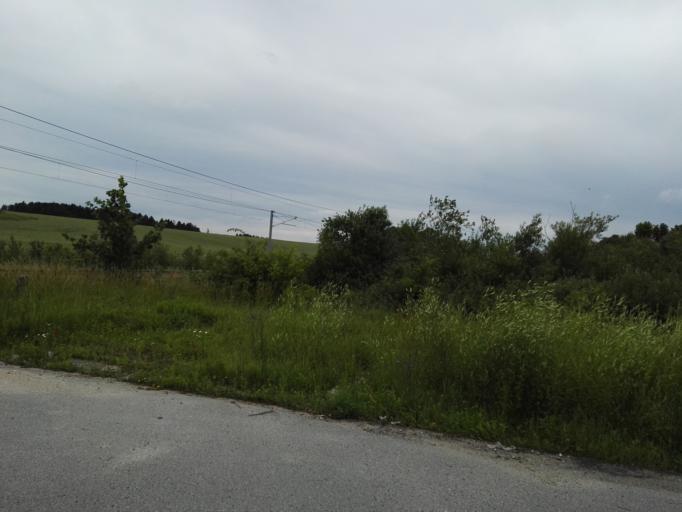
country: DK
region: Capital Region
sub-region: Egedal Kommune
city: Vekso
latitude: 55.7503
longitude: 12.2378
